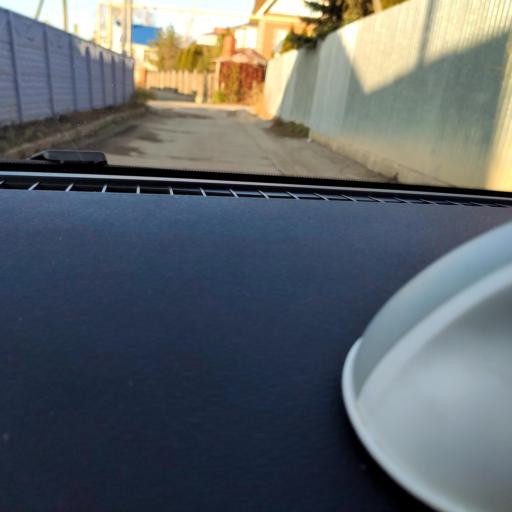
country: RU
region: Samara
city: Samara
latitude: 53.2282
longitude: 50.1583
